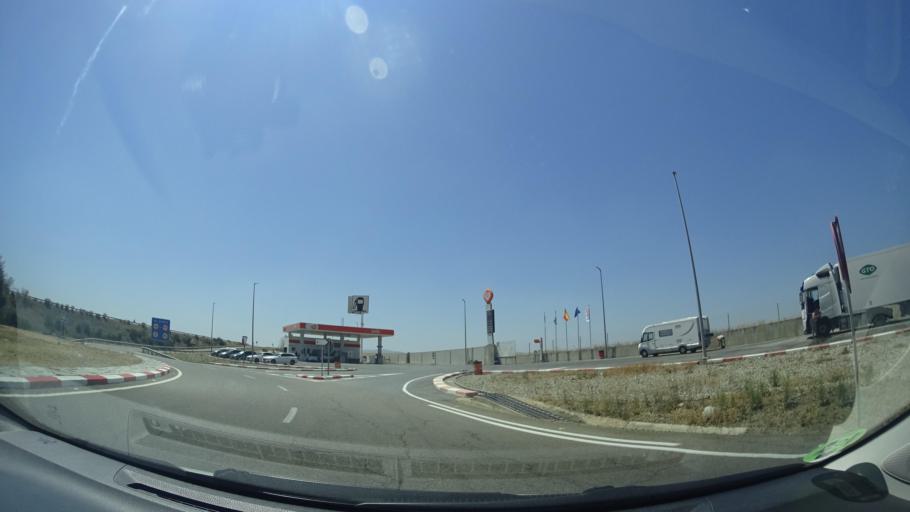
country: ES
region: Extremadura
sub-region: Provincia de Badajoz
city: Fuente de Cantos
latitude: 38.2309
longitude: -6.2968
